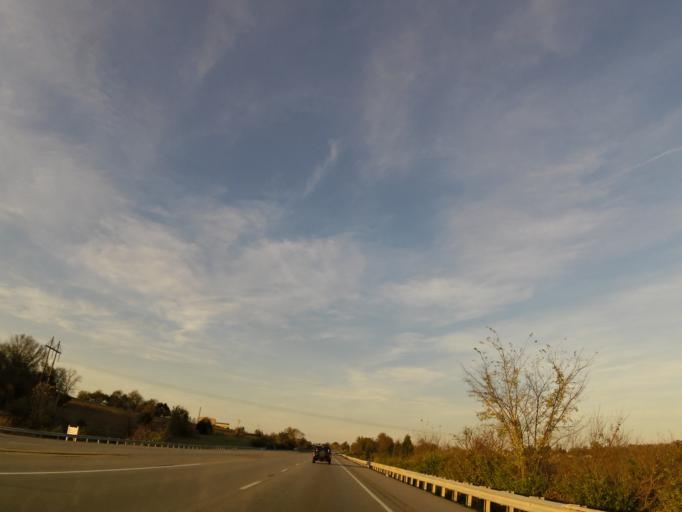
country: US
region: Kentucky
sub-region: Jessamine County
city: Wilmore
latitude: 37.7781
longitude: -84.6107
